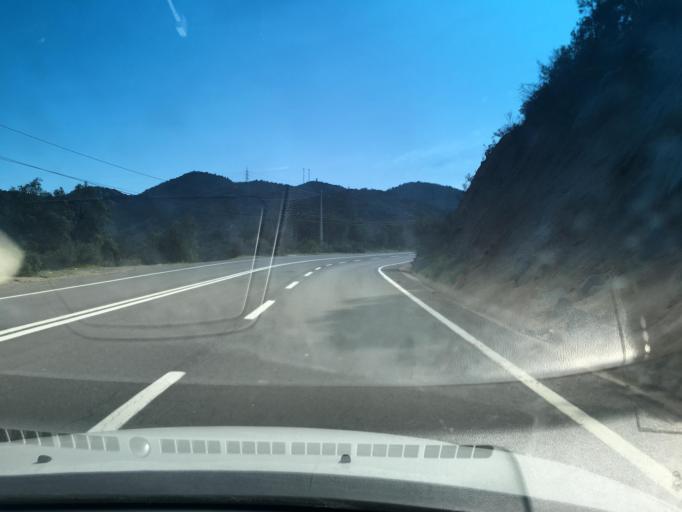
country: CL
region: Valparaiso
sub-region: Provincia de San Felipe
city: Llaillay
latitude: -33.0658
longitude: -70.9974
